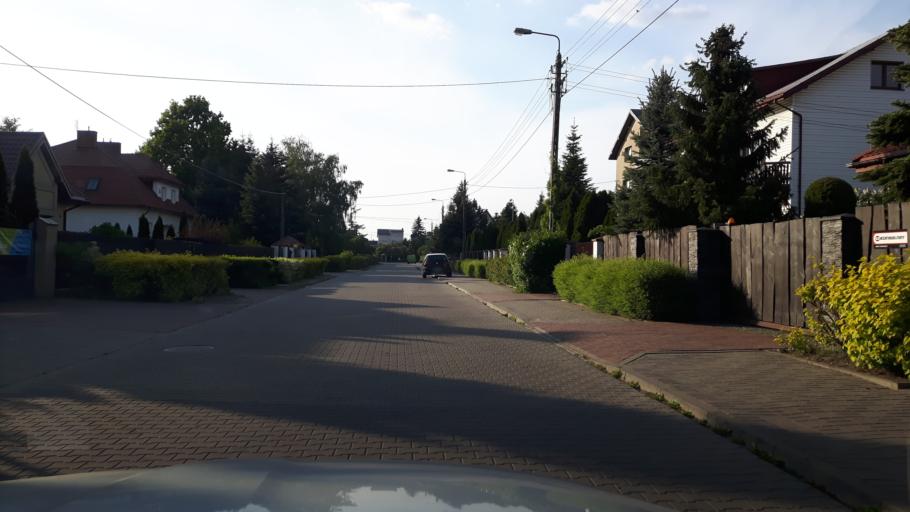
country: PL
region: Masovian Voivodeship
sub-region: Warszawa
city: Rembertow
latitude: 52.2635
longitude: 21.1624
